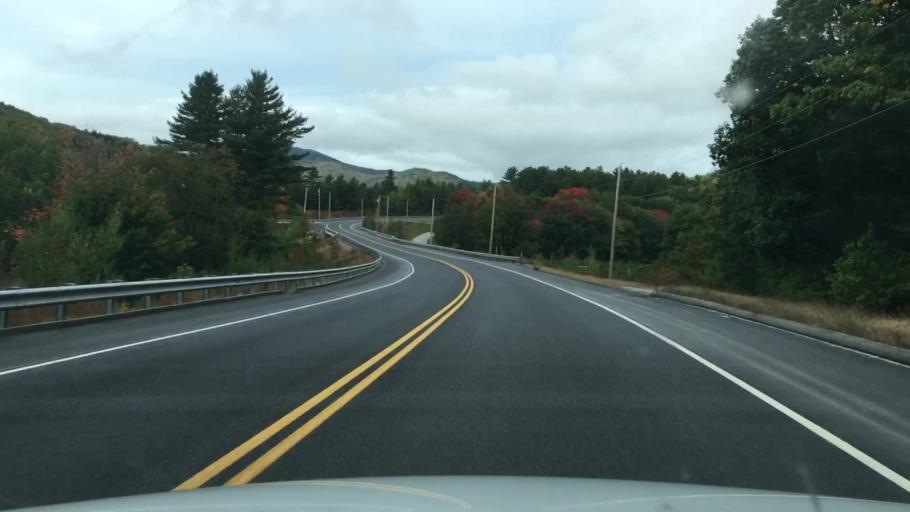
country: US
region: Maine
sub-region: Oxford County
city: Bethel
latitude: 44.4002
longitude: -70.8724
